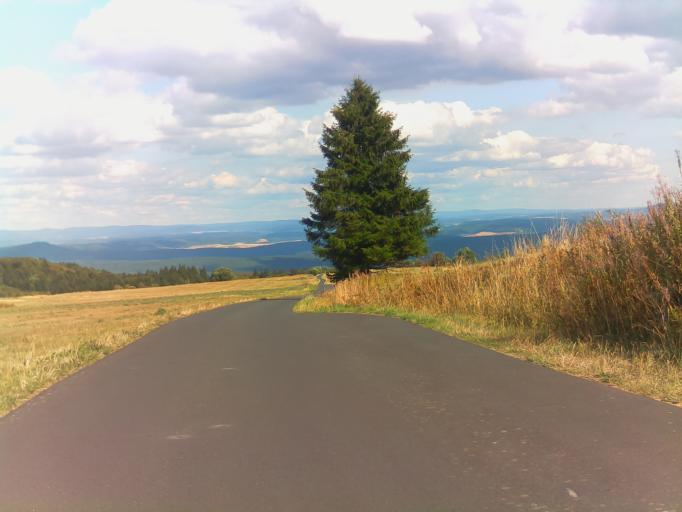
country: DE
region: Thuringia
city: Birx
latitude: 50.4991
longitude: 10.0680
